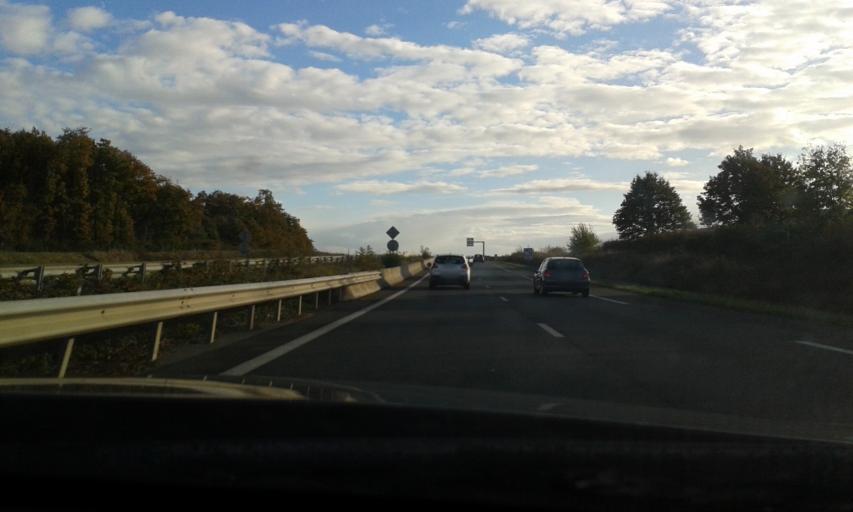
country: FR
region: Centre
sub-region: Departement d'Eure-et-Loir
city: Villemeux-sur-Eure
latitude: 48.6116
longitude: 1.4192
